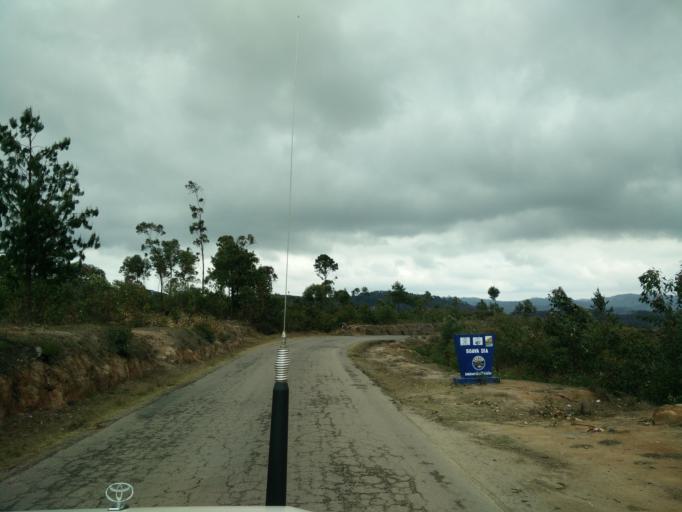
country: MG
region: Upper Matsiatra
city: Fianarantsoa
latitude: -21.2471
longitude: 47.2417
